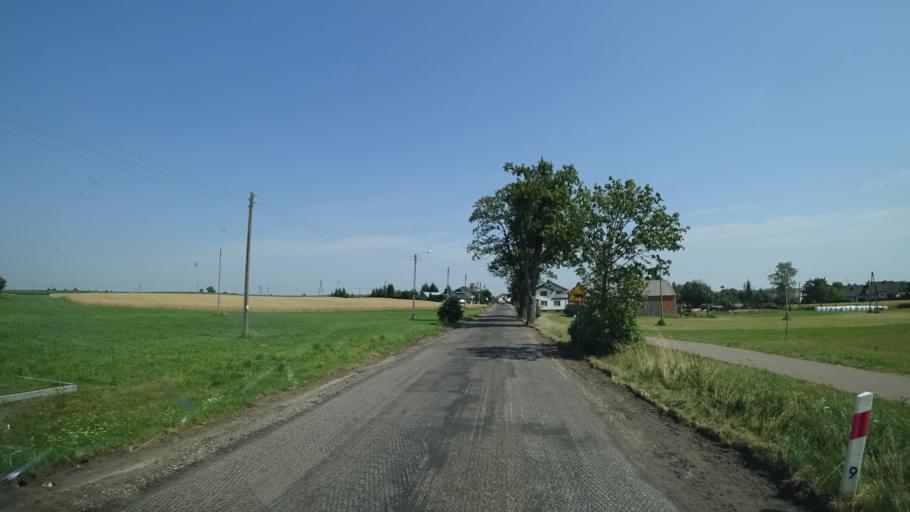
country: PL
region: Pomeranian Voivodeship
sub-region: Powiat chojnicki
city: Brusy
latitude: 53.8778
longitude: 17.6907
